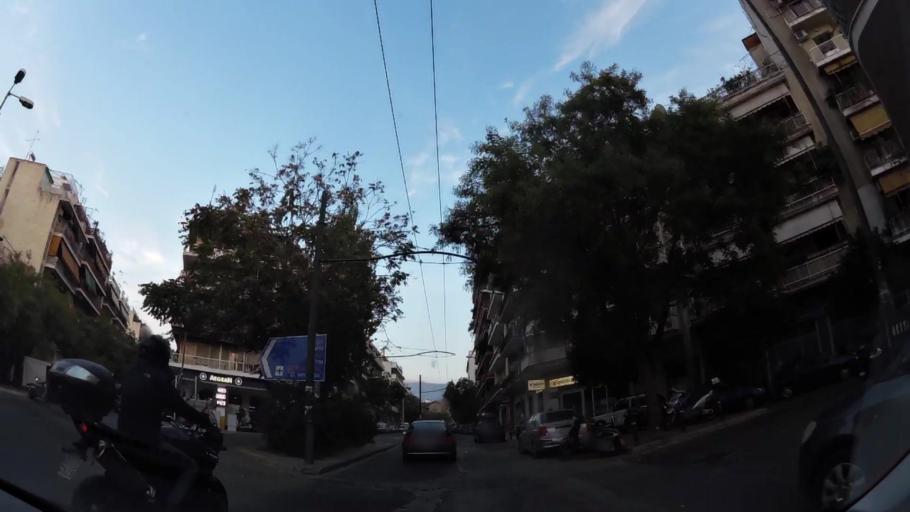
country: GR
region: Attica
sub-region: Nomarchia Athinas
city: Dhafni
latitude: 37.9571
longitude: 23.7323
